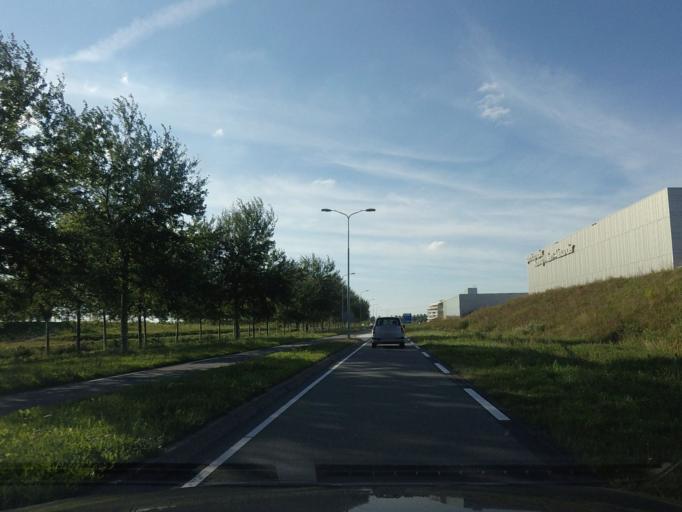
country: NL
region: North Holland
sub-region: Gemeente Bloemendaal
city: Bennebroek
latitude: 52.3004
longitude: 4.6316
